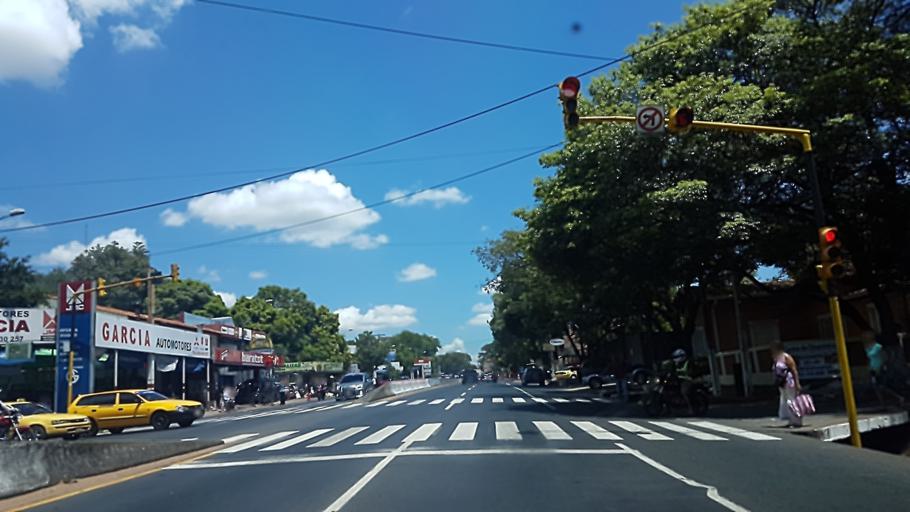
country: PY
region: Central
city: Capiata
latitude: -25.3514
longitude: -57.4463
